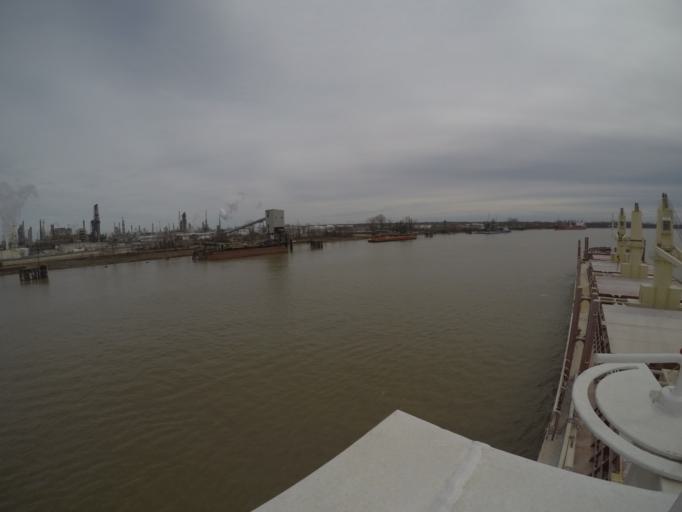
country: US
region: Louisiana
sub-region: Saint Charles Parish
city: Norco
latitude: 29.9891
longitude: -90.4053
